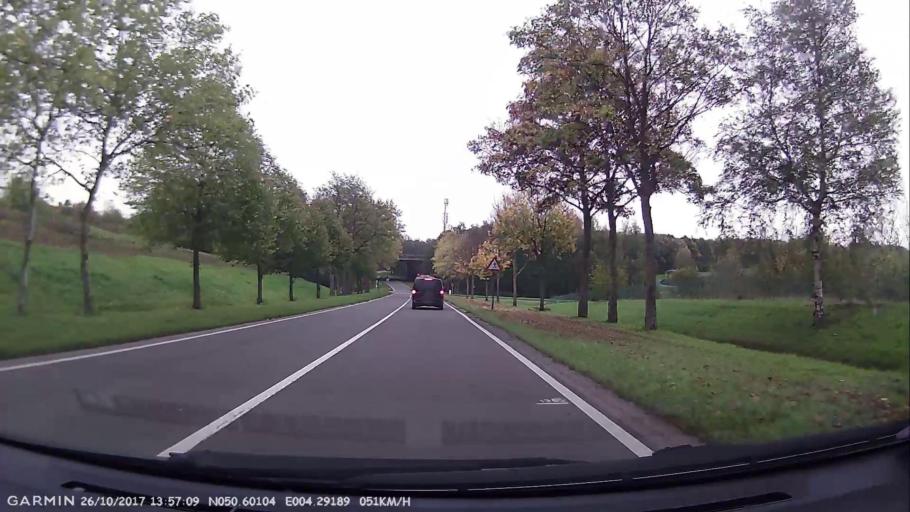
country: BE
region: Wallonia
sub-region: Province du Brabant Wallon
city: Nivelles
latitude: 50.6010
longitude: 4.2922
